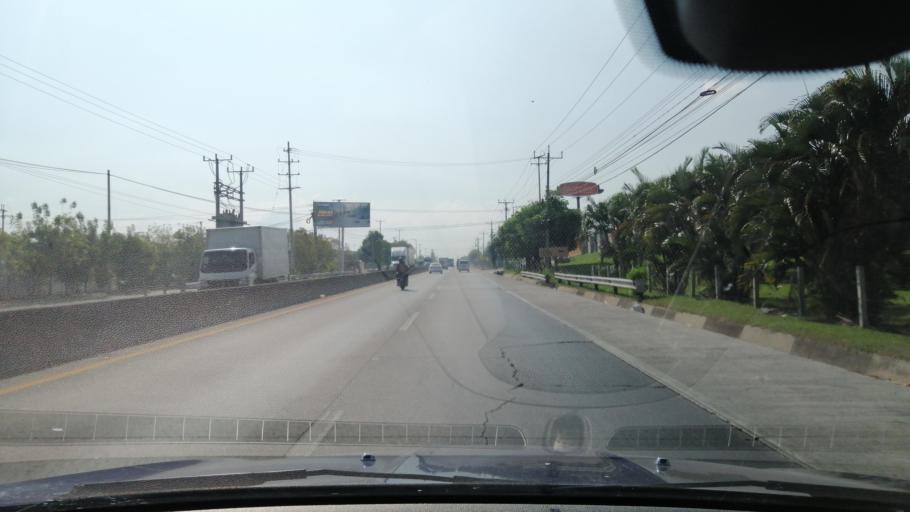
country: SV
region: La Libertad
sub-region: Distrito de Quezaltepeque
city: Quezaltepeque
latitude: 13.8021
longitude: -89.2343
